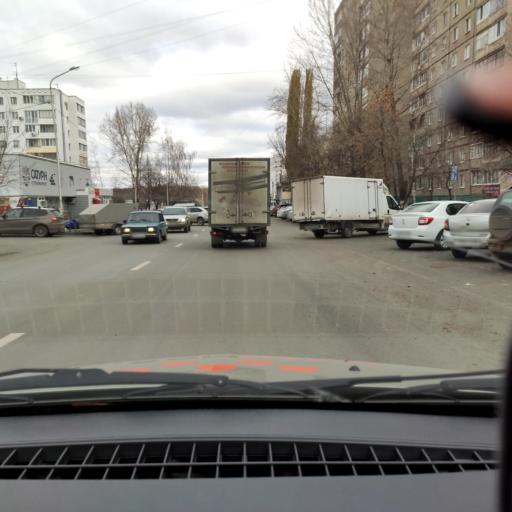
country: RU
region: Bashkortostan
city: Ufa
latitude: 54.7197
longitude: 55.9975
